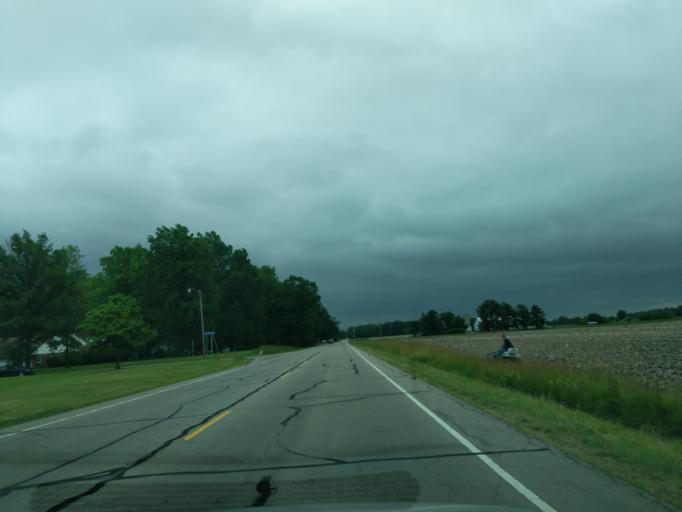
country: US
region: Indiana
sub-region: Madison County
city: Alexandria
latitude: 40.2773
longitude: -85.6177
